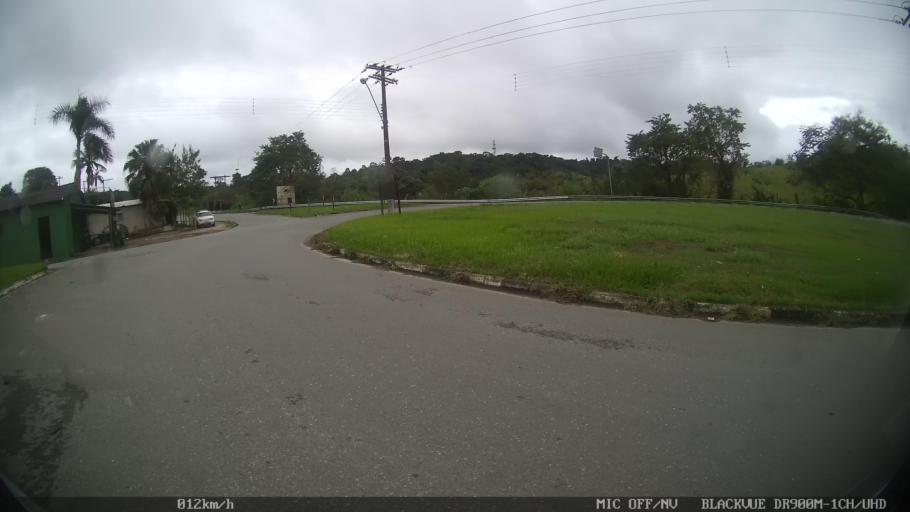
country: BR
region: Sao Paulo
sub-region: Juquia
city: Juquia
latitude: -24.3127
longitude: -47.6252
